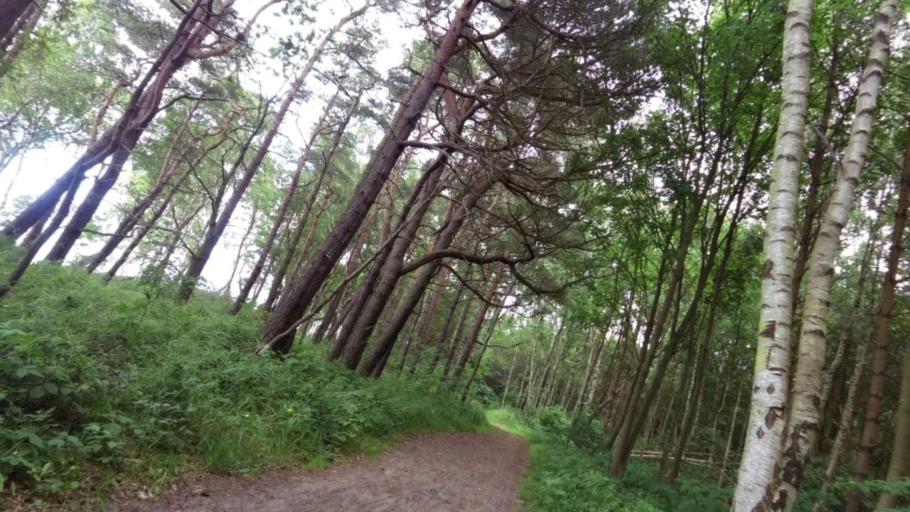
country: PL
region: West Pomeranian Voivodeship
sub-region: Powiat kamienski
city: Dziwnow
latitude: 54.0452
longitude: 14.8454
